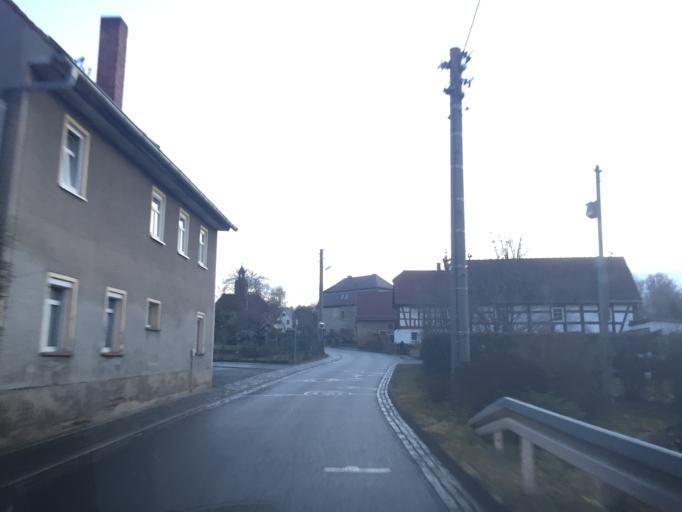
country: DE
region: Thuringia
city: Schmolln
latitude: 50.8780
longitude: 12.3316
